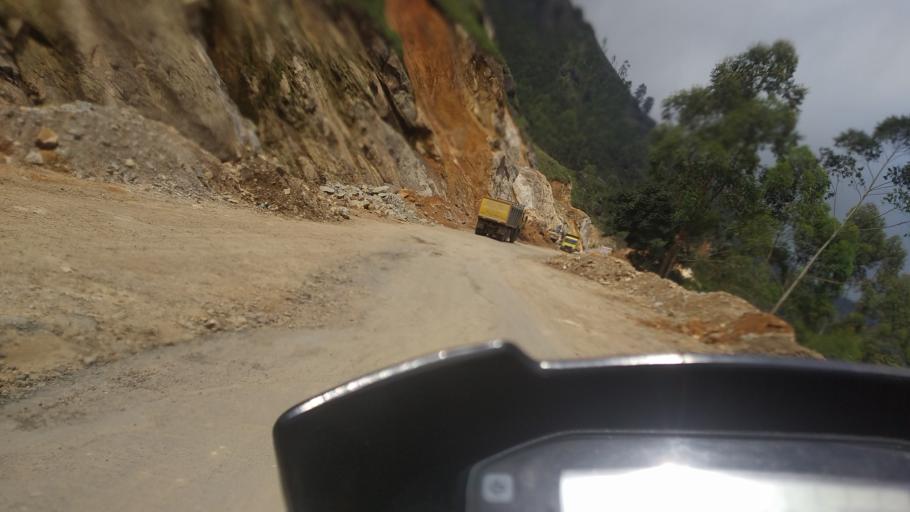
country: IN
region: Kerala
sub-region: Idukki
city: Munnar
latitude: 10.0367
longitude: 77.1238
